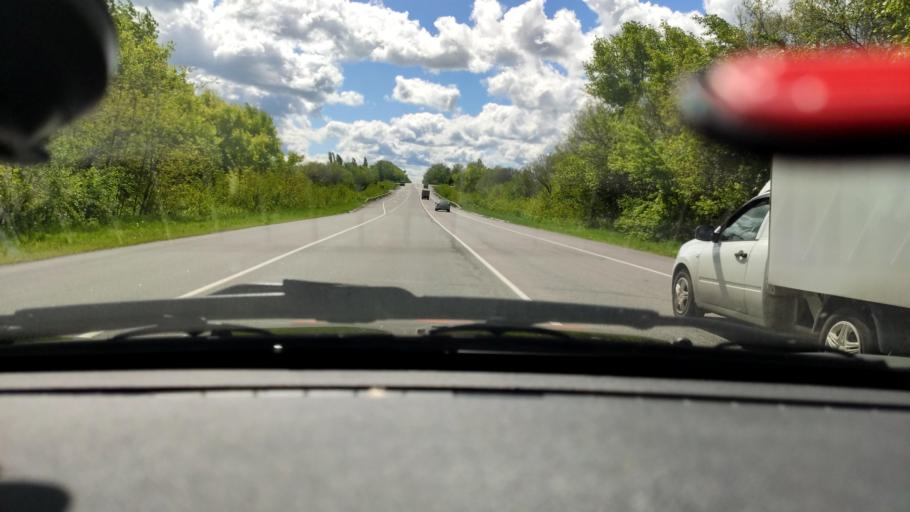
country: RU
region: Voronezj
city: Uryv-Pokrovka
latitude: 51.2083
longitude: 39.0749
